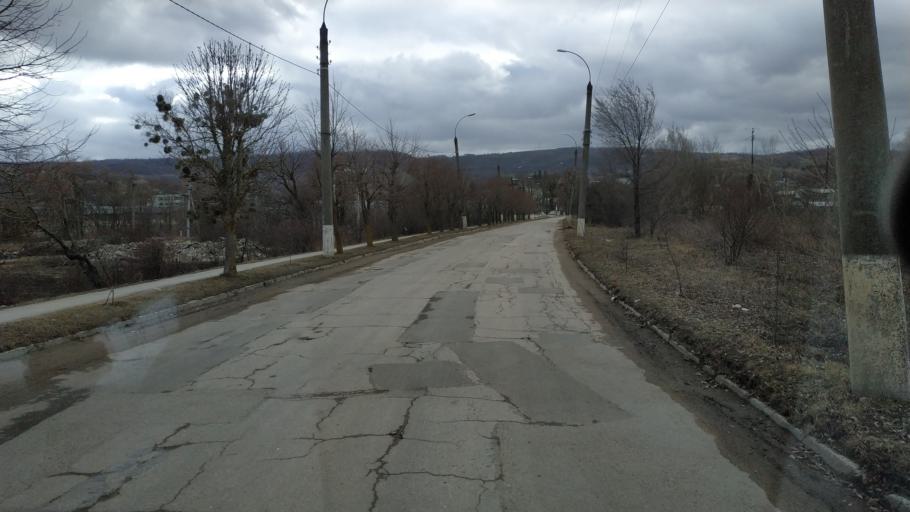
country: MD
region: Calarasi
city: Calarasi
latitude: 47.2457
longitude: 28.3163
